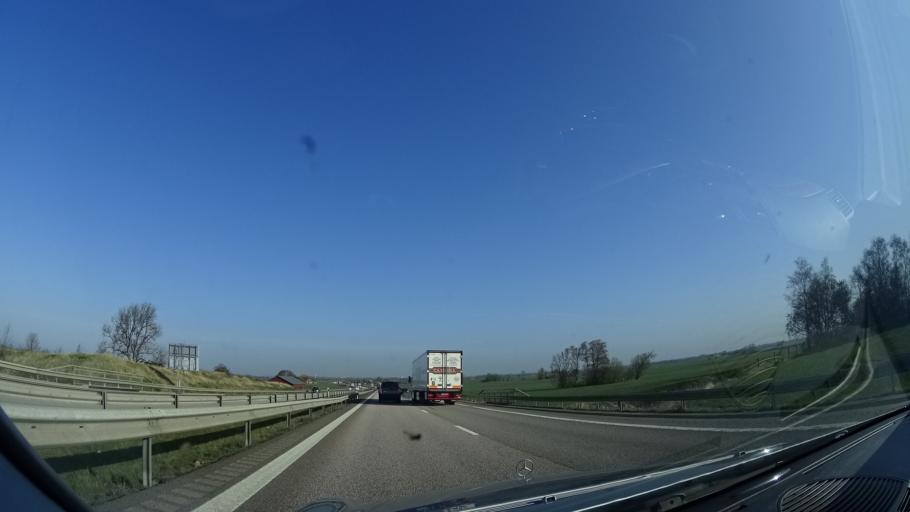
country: SE
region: Skane
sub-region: Helsingborg
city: Glumslov
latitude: 55.9546
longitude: 12.8051
